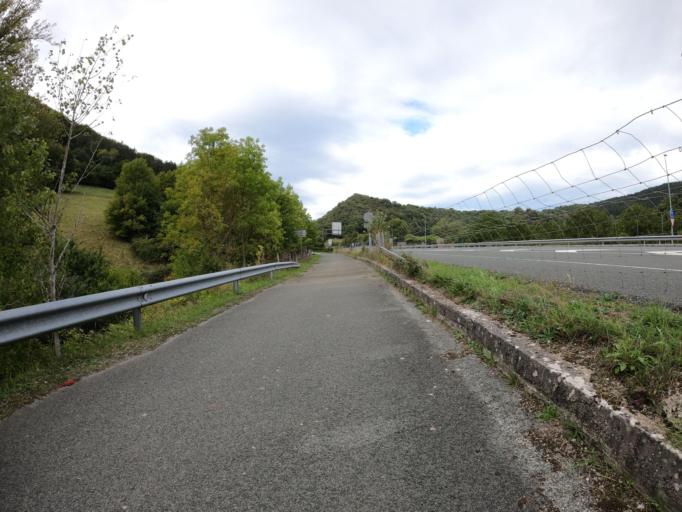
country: ES
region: Navarre
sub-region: Provincia de Navarra
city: Irurtzun
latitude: 42.9632
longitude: -1.8330
